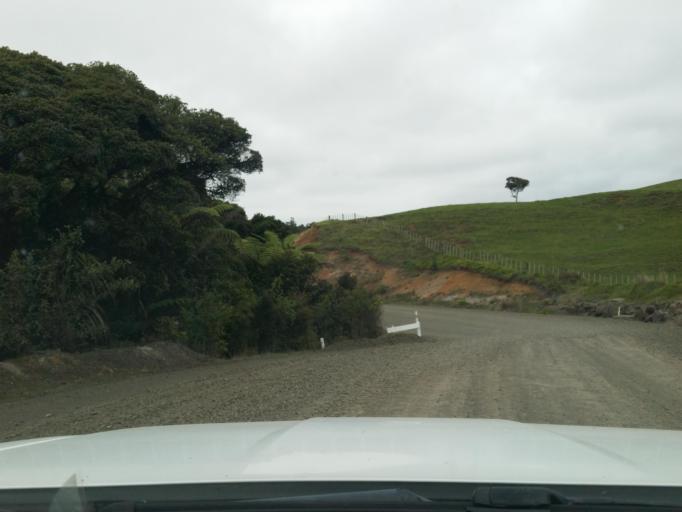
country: NZ
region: Northland
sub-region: Kaipara District
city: Dargaville
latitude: -35.7130
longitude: 173.6362
